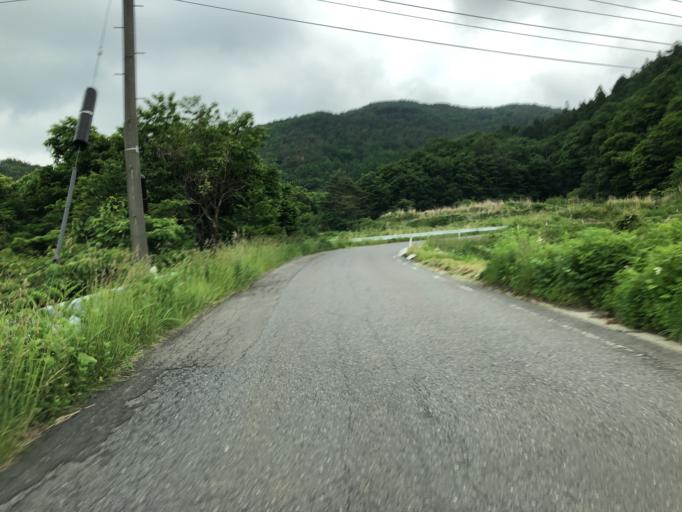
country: JP
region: Fukushima
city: Funehikimachi-funehiki
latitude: 37.3898
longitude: 140.7036
